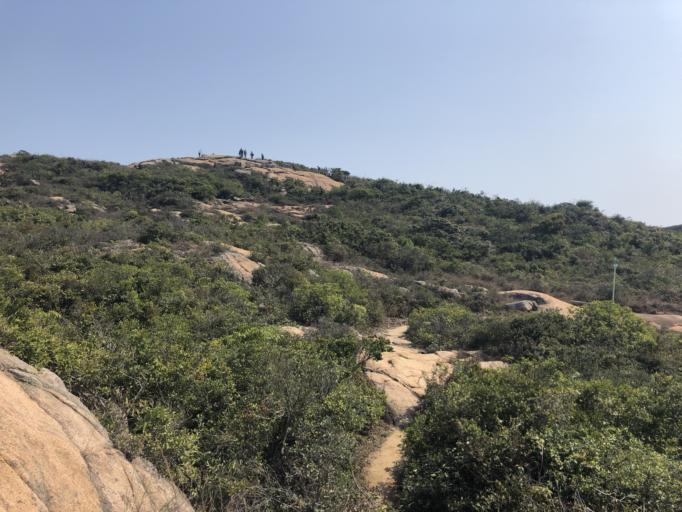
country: HK
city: Sok Kwu Wan
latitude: 22.1693
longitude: 114.2573
